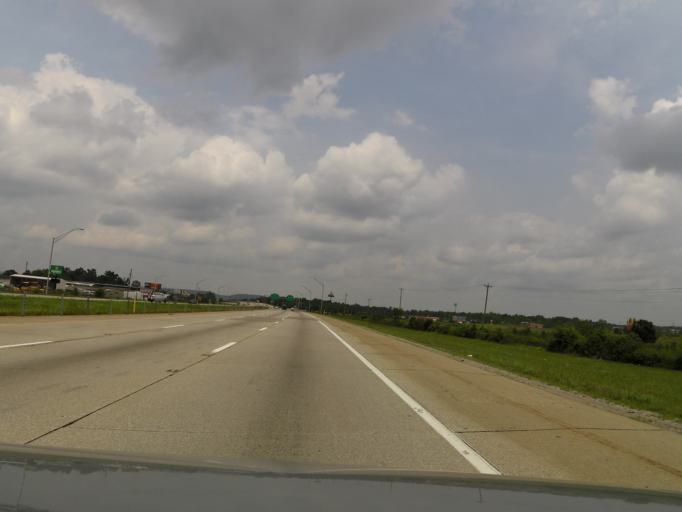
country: US
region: Kentucky
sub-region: Bullitt County
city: Shepherdsville
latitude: 37.9714
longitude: -85.6953
